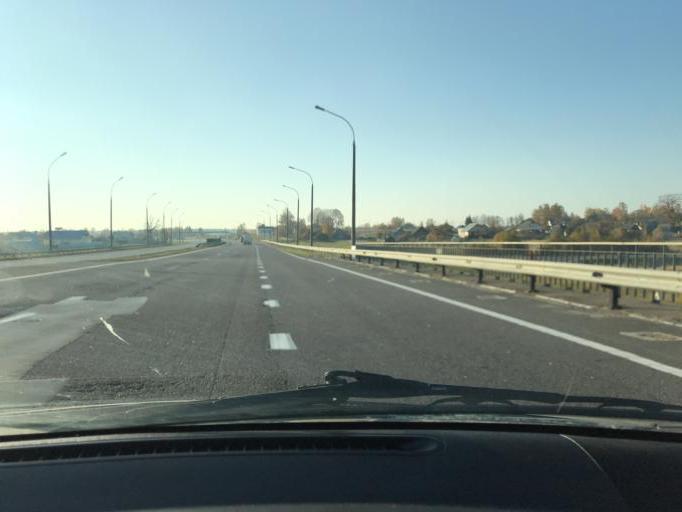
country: BY
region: Minsk
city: Loshnitsa
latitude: 54.2919
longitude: 28.7682
